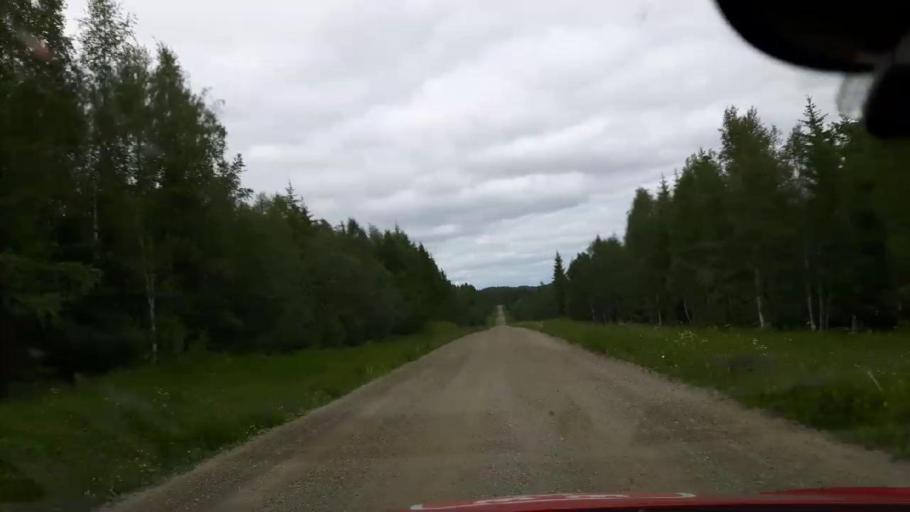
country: SE
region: Jaemtland
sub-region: OEstersunds Kommun
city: Brunflo
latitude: 62.9344
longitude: 14.9953
